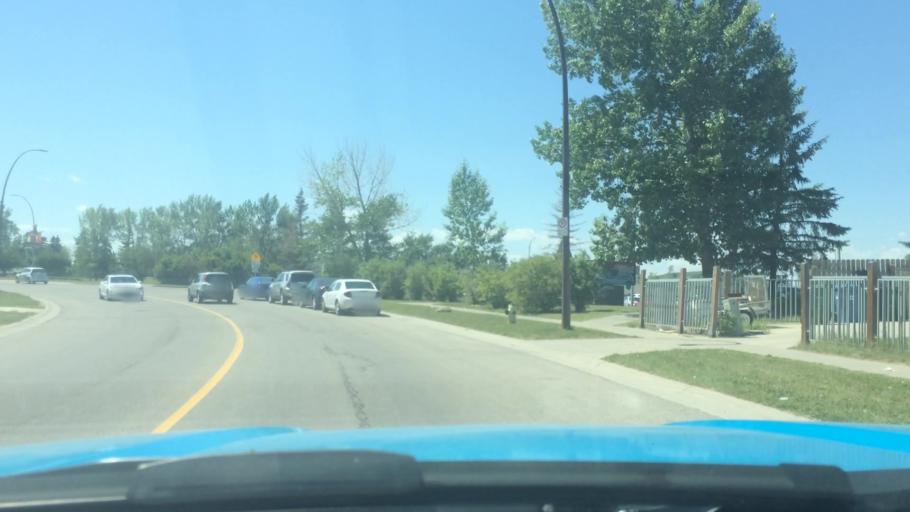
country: CA
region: Alberta
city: Calgary
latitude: 51.0466
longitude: -113.9925
